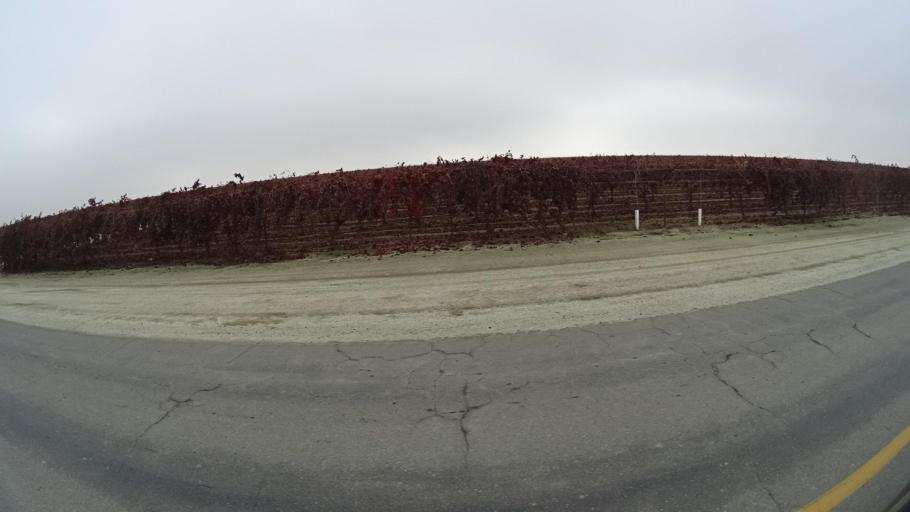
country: US
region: California
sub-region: Kern County
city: Greenfield
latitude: 35.0942
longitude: -119.1611
